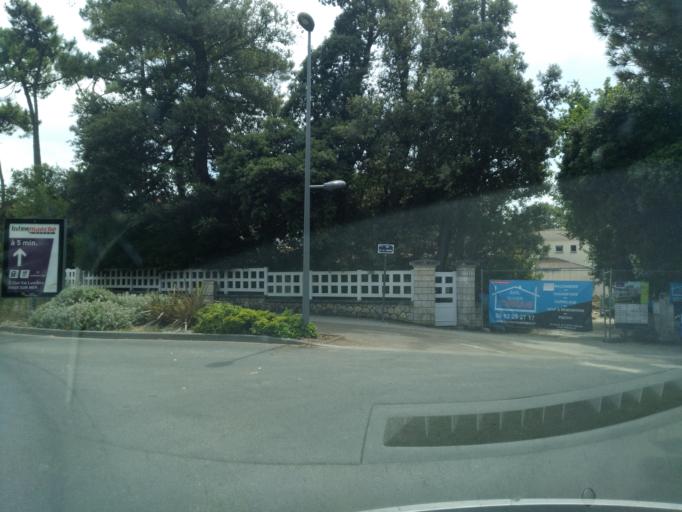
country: FR
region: Poitou-Charentes
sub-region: Departement de la Charente-Maritime
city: Saint-Palais-sur-Mer
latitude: 45.6400
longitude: -1.0838
